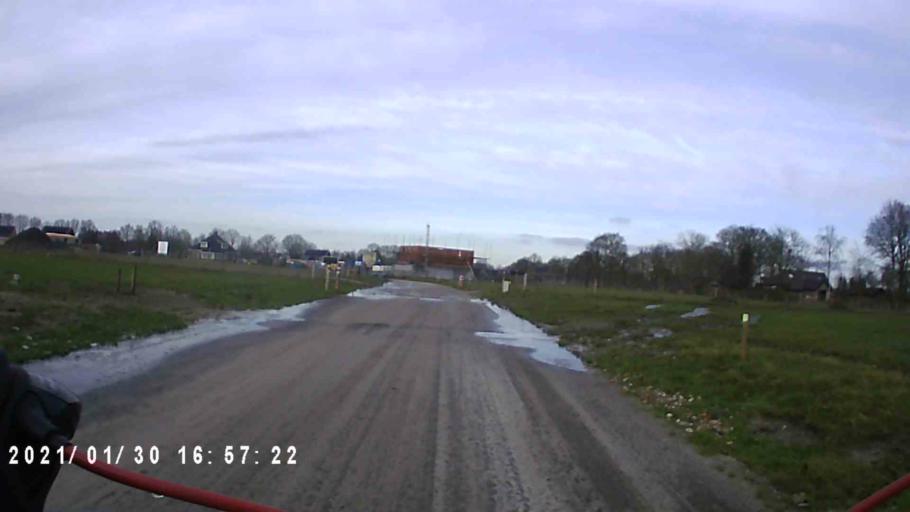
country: NL
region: Groningen
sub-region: Gemeente Leek
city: Leek
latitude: 53.1503
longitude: 6.3800
